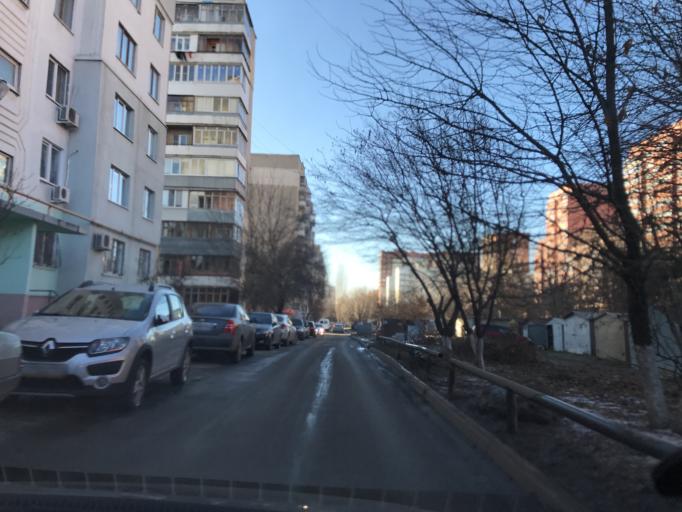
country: RU
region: Rostov
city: Rostov-na-Donu
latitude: 47.2146
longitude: 39.6221
